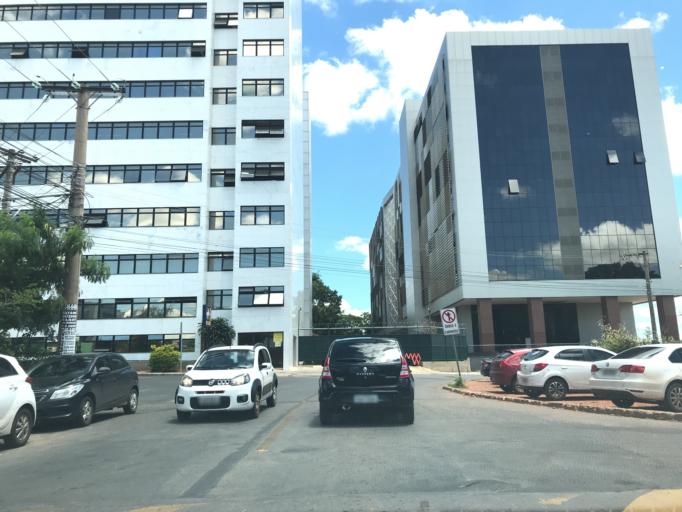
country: BR
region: Federal District
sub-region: Brasilia
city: Brasilia
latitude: -15.7887
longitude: -47.9086
